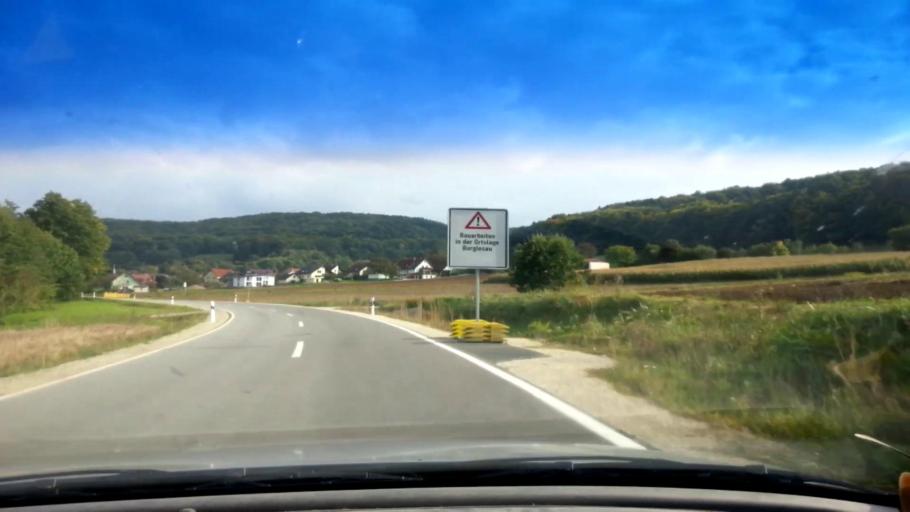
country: DE
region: Bavaria
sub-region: Upper Franconia
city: Schesslitz
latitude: 49.9986
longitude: 11.0726
